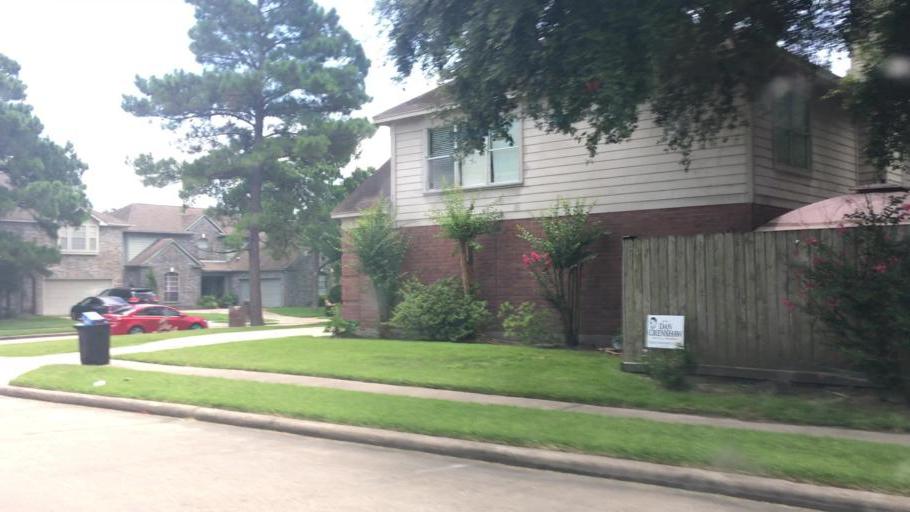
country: US
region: Texas
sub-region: Harris County
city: Atascocita
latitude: 29.9942
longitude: -95.1736
